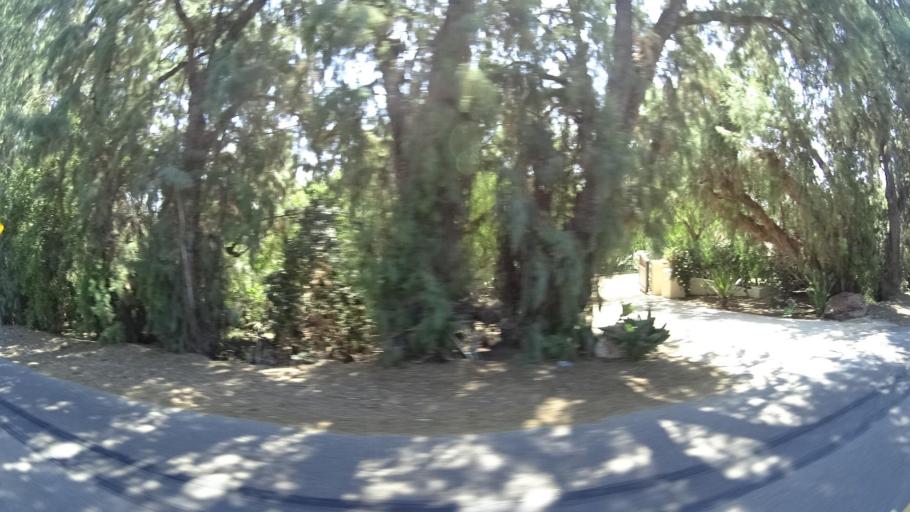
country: US
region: California
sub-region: San Diego County
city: Rancho Santa Fe
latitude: 33.0173
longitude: -117.1848
